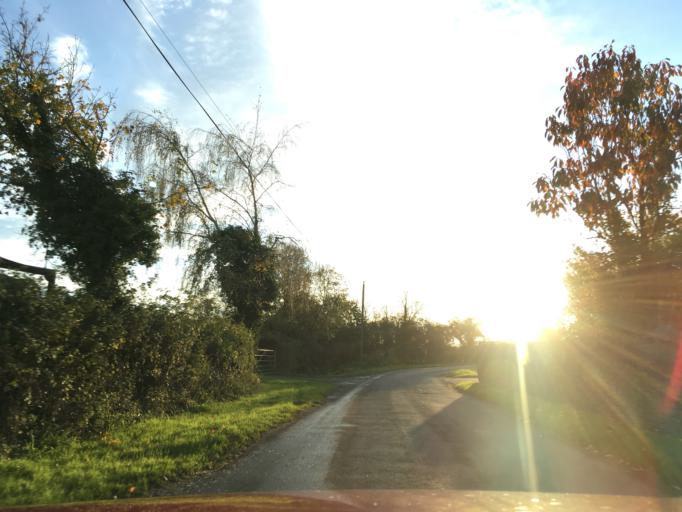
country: GB
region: England
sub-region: South Gloucestershire
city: Hill
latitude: 51.6496
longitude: -2.5551
